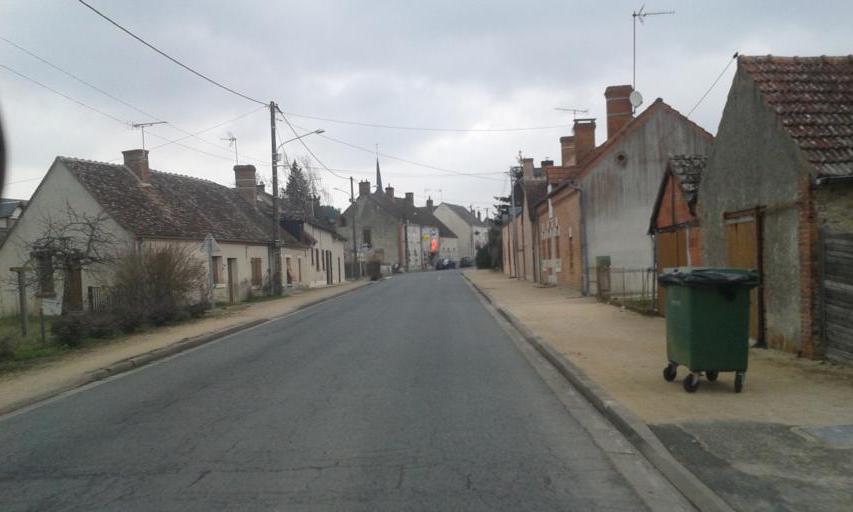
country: FR
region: Centre
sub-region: Departement du Loir-et-Cher
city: Dhuizon
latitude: 47.5871
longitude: 1.6585
